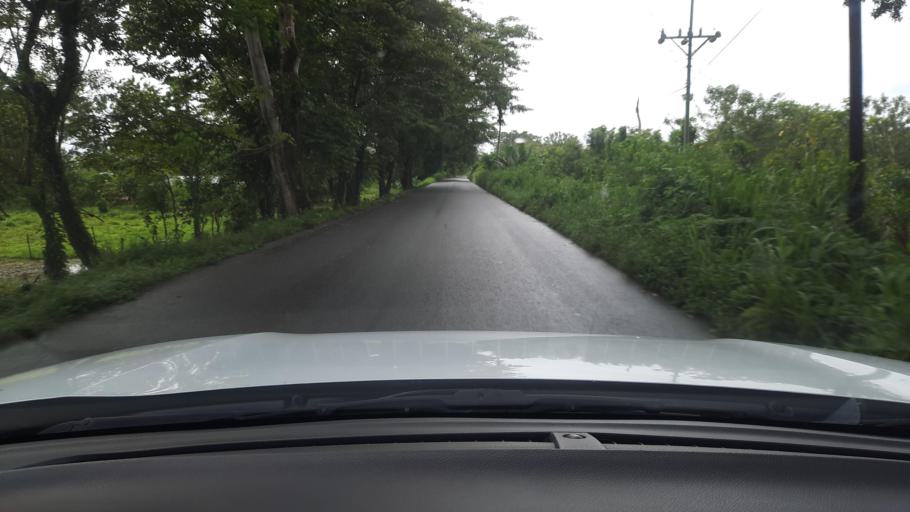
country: CR
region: Alajuela
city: San Jose
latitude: 10.9282
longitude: -85.0803
